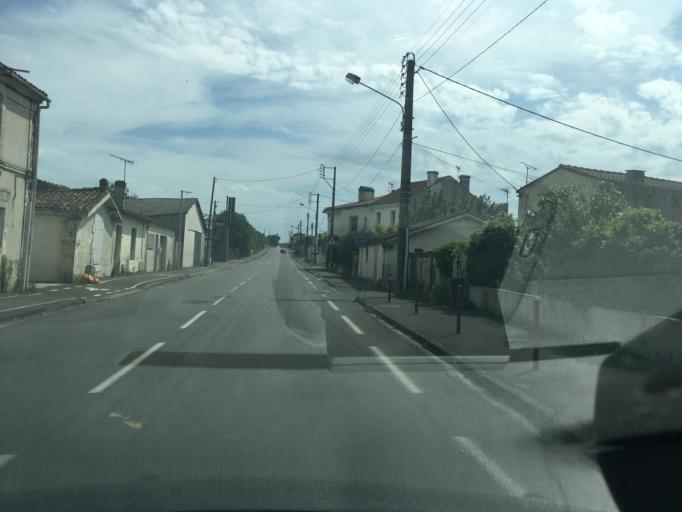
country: FR
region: Poitou-Charentes
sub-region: Departement de la Charente
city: Chateaubernard
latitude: 45.6802
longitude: -0.3284
